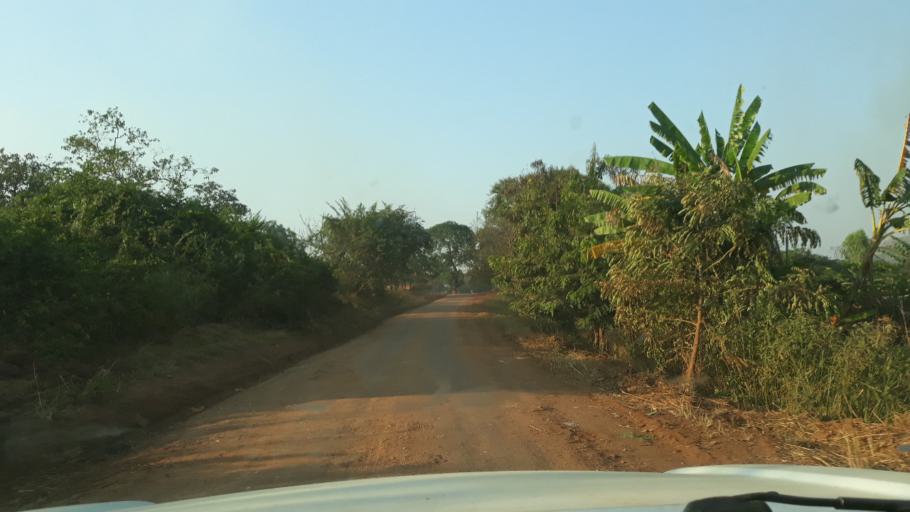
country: BI
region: Bururi
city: Rumonge
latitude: -4.2258
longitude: 28.9938
